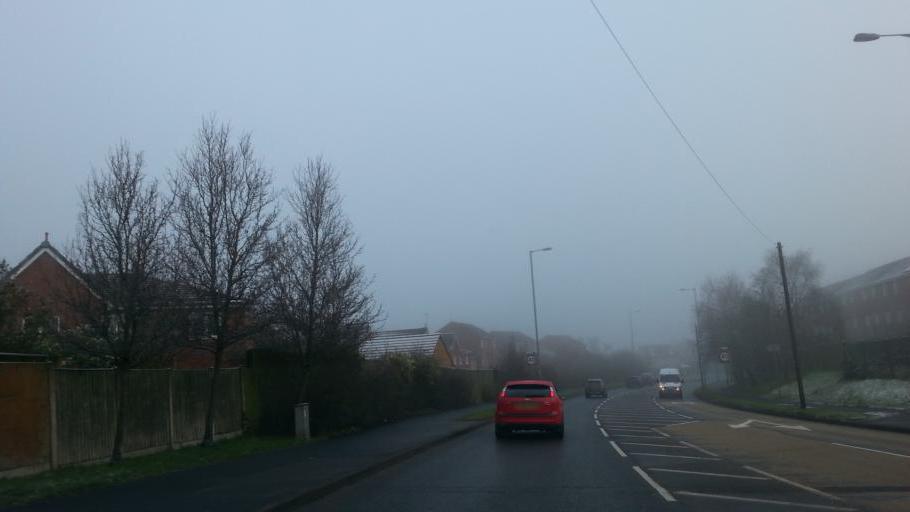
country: GB
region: England
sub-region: Staffordshire
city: Biddulph
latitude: 53.1190
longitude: -2.1755
